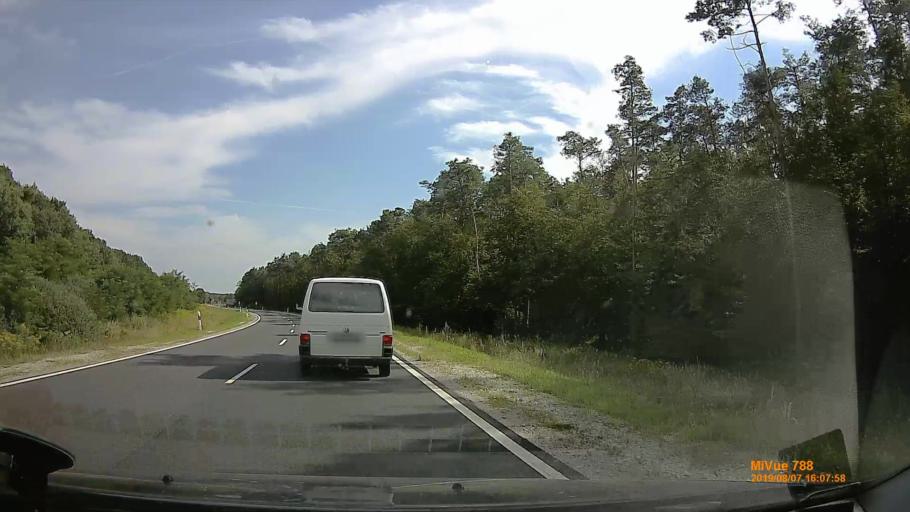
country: HU
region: Zala
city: Zalalovo
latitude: 46.9145
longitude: 16.5986
